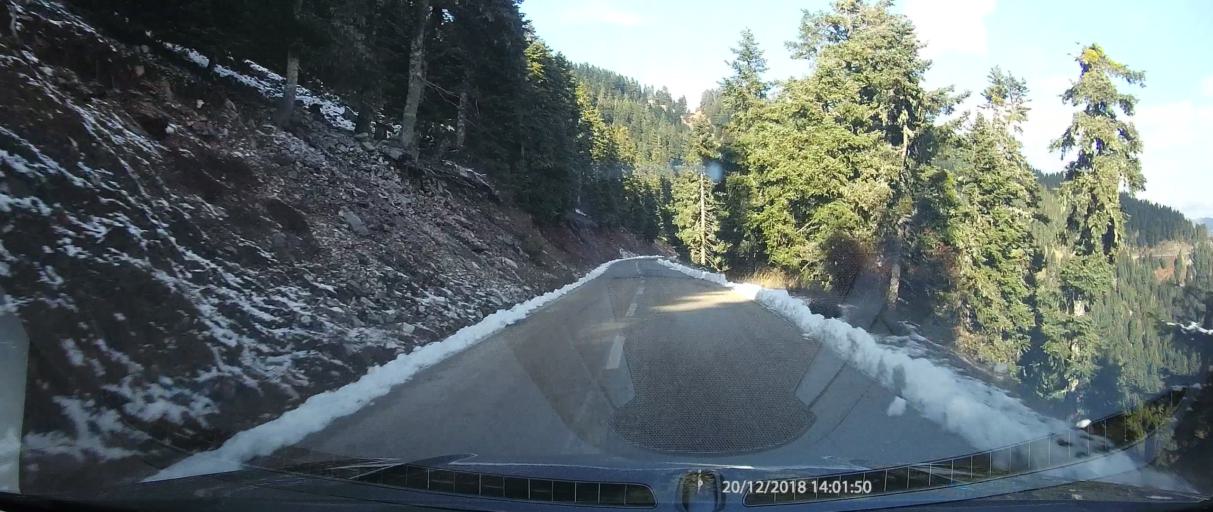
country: GR
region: West Greece
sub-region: Nomos Aitolias kai Akarnanias
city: Thermo
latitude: 38.7326
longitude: 21.6331
